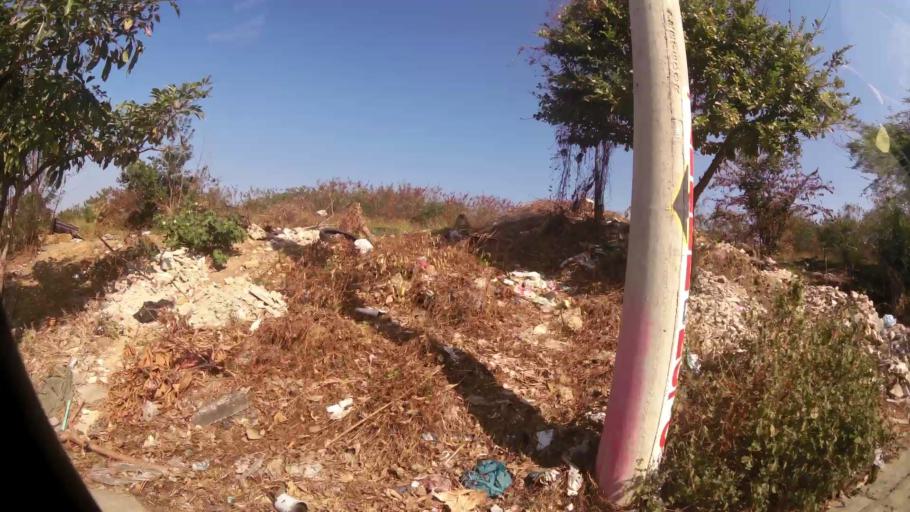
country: CO
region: Atlantico
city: Barranquilla
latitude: 10.9827
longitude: -74.8258
